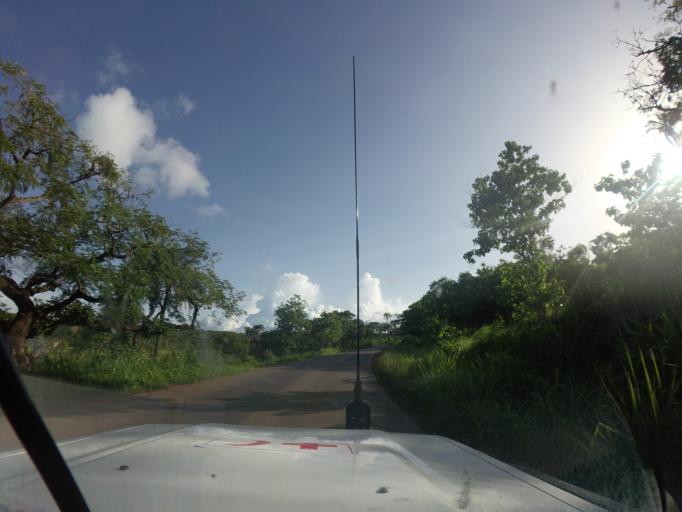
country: GN
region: Kindia
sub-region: Kindia
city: Kindia
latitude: 10.0194
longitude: -12.8176
